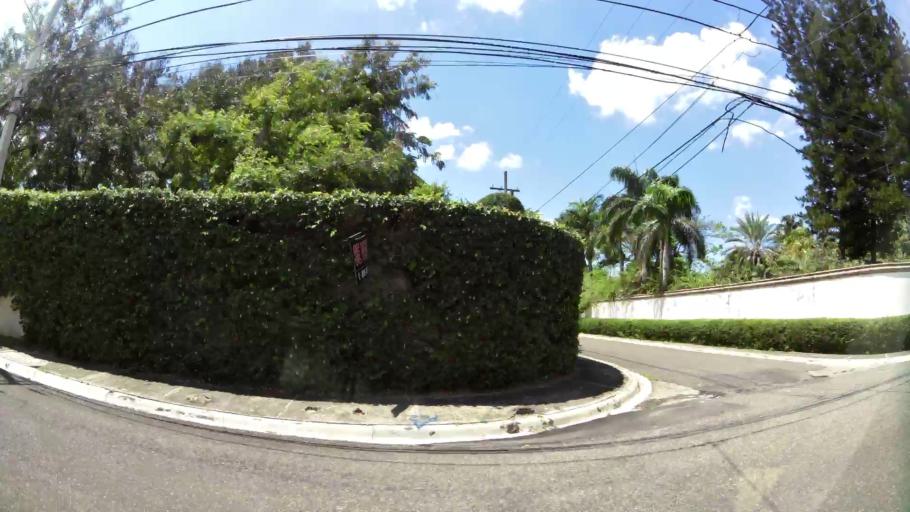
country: DO
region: Santiago
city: Santiago de los Caballeros
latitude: 19.4652
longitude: -70.6775
